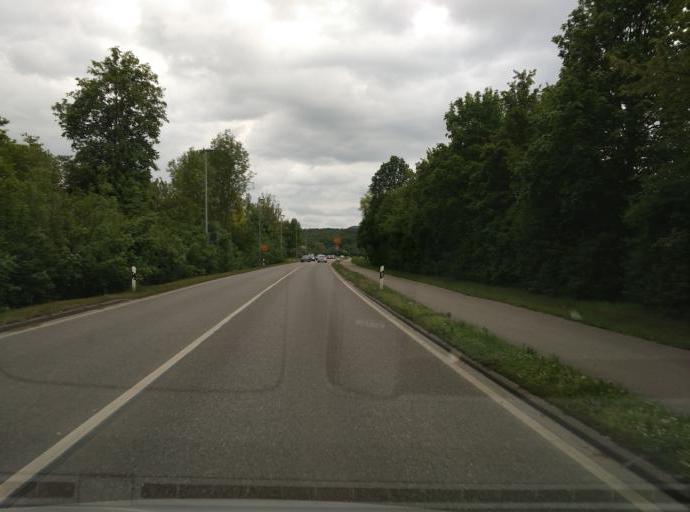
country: DE
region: Baden-Wuerttemberg
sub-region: Regierungsbezirk Stuttgart
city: Frickenhausen
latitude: 48.6078
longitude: 9.3498
